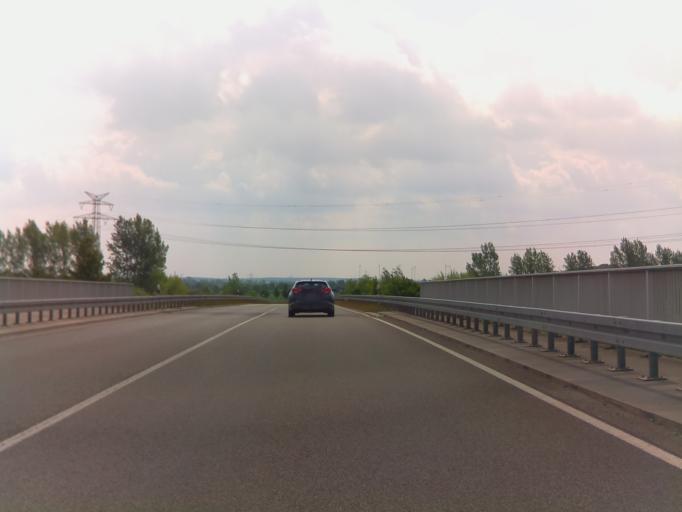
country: DE
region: Saxony-Anhalt
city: Luderitz
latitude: 52.5728
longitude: 11.6926
